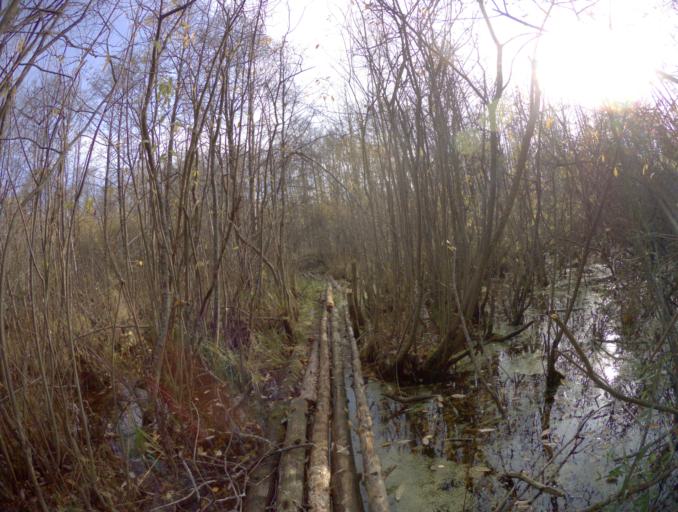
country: RU
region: Vladimir
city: Kommunar
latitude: 56.1160
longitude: 40.4687
